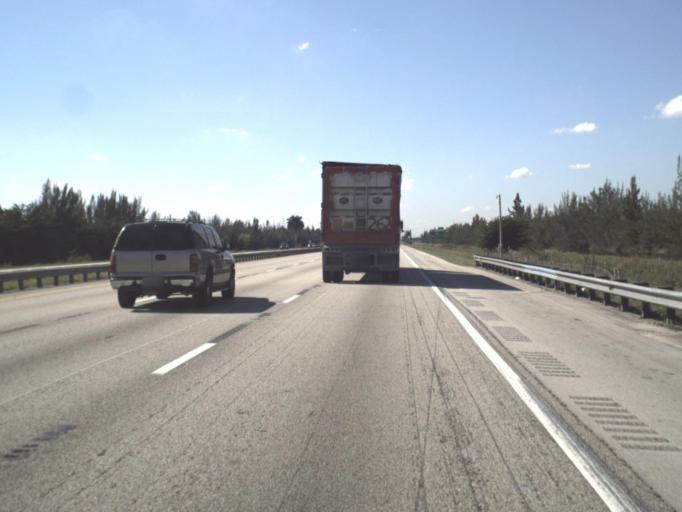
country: US
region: Florida
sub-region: Miami-Dade County
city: Palm Springs North
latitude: 25.9243
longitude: -80.3769
